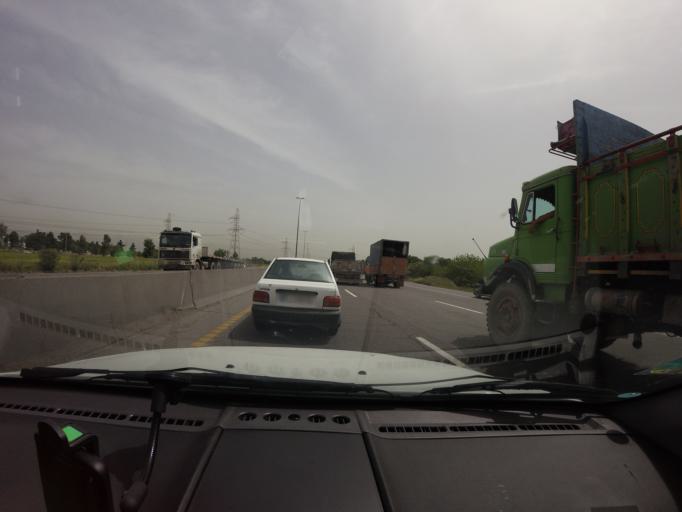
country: IR
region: Tehran
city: Eslamshahr
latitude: 35.6159
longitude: 51.2153
